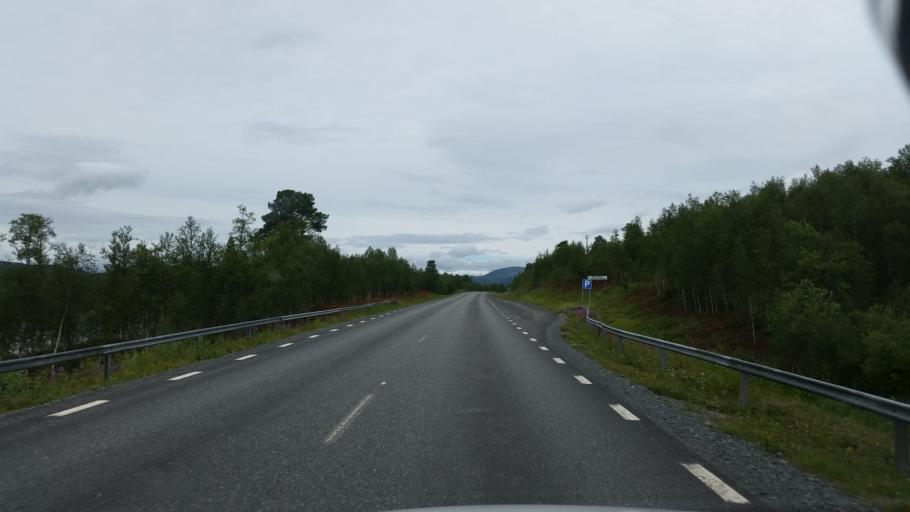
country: NO
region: Nordland
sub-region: Sorfold
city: Straumen
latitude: 66.5395
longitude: 16.3329
